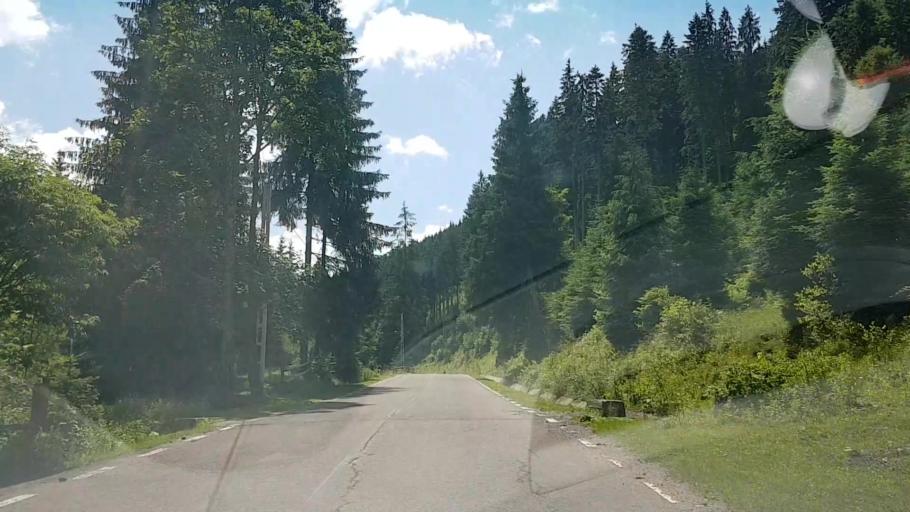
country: RO
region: Suceava
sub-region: Comuna Sadova
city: Sadova
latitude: 47.4812
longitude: 25.4925
